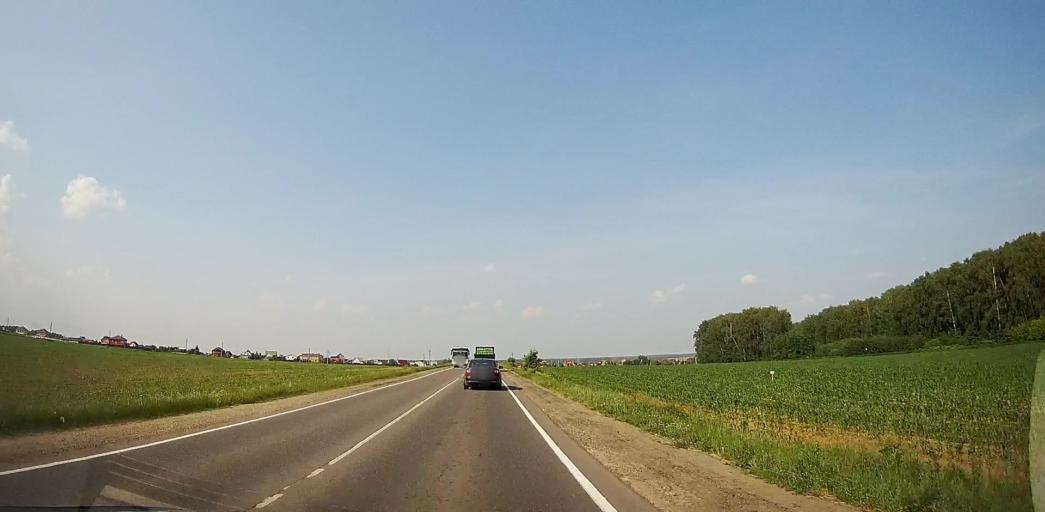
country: RU
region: Moskovskaya
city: Zhitnevo
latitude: 55.3323
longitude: 37.9056
